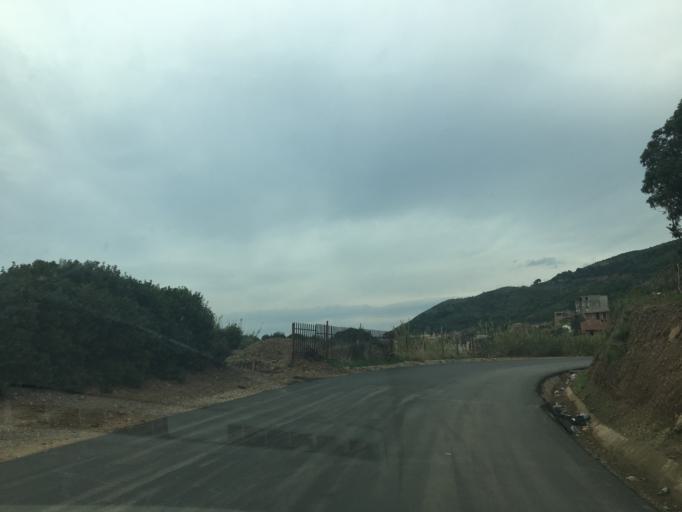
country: DZ
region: Tipaza
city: Tipasa
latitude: 36.6368
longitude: 2.3096
